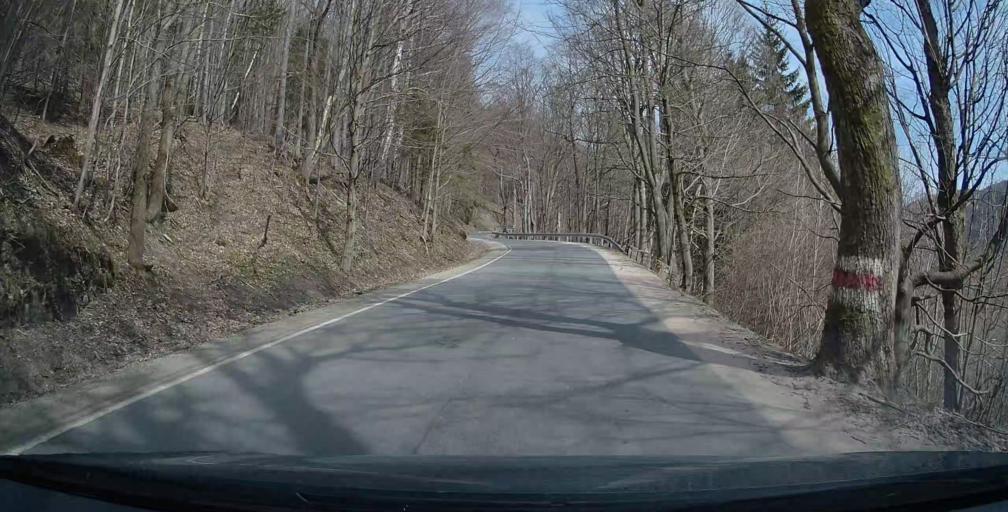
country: CZ
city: Machov
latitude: 50.4622
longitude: 16.3150
